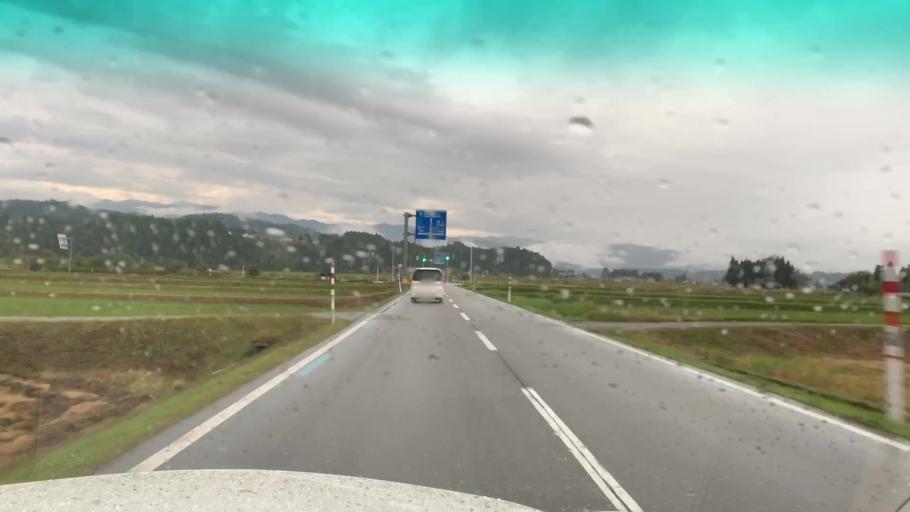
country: JP
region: Toyama
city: Kamiichi
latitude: 36.6271
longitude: 137.3286
